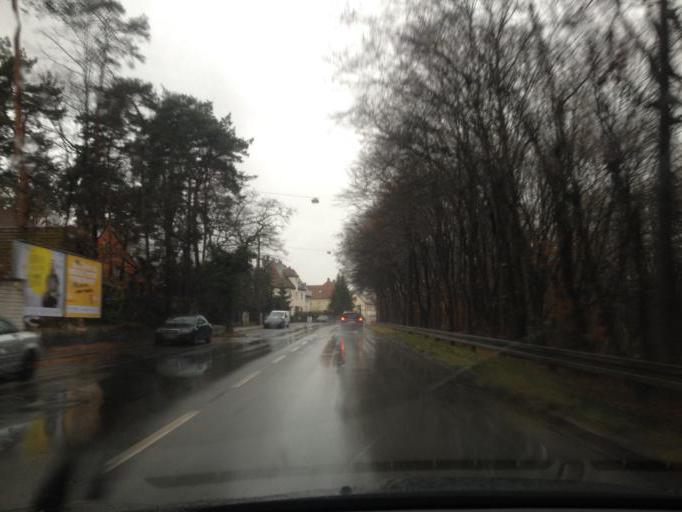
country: DE
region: Bavaria
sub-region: Regierungsbezirk Mittelfranken
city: Schwaig
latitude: 49.4689
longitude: 11.1710
